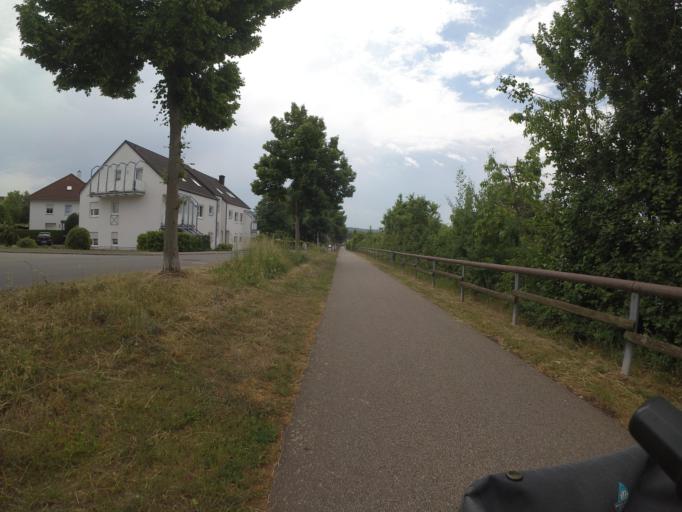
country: DE
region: Rheinland-Pfalz
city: Wittlich
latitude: 49.9929
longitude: 6.8900
